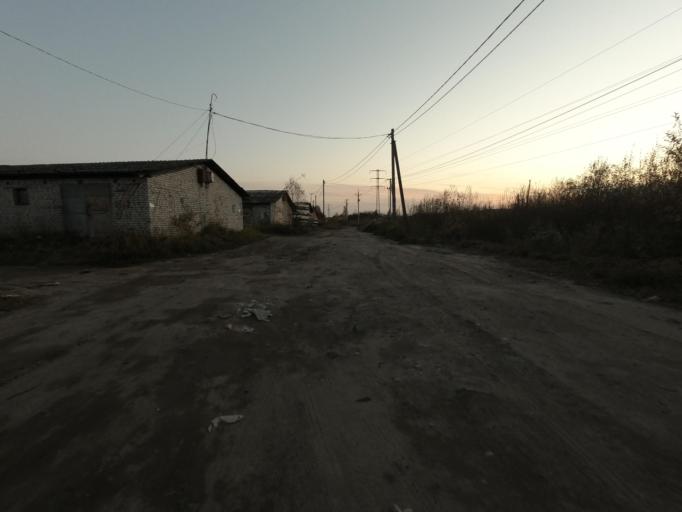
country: RU
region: Leningrad
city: Kirovsk
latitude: 59.8743
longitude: 31.0031
